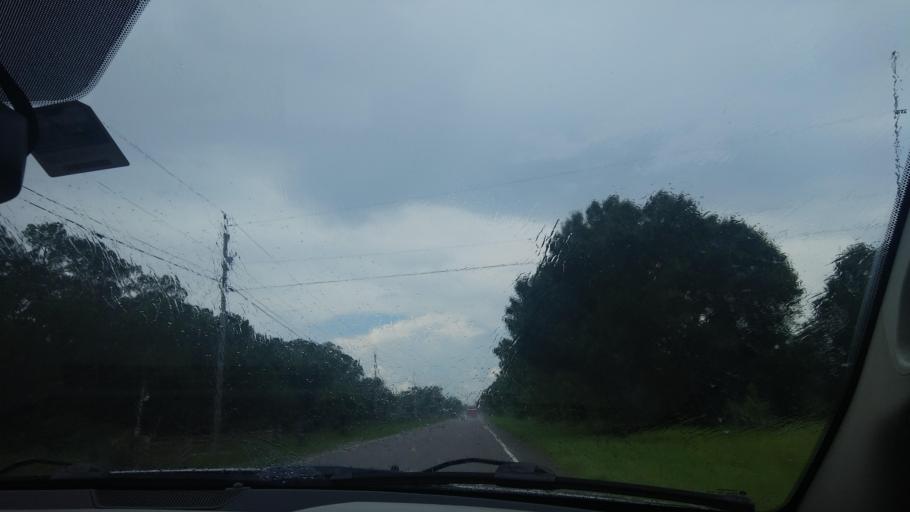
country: US
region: Florida
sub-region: Indian River County
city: Fellsmere
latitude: 27.8086
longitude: -80.6073
